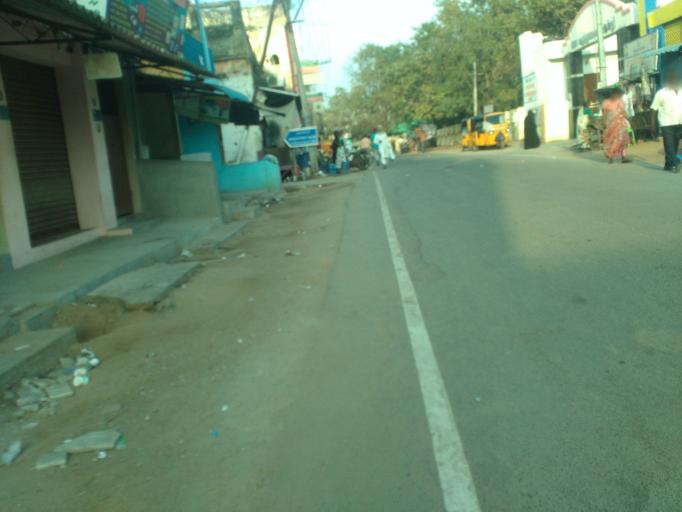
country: IN
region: Tamil Nadu
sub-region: Vellore
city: Ambur
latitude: 12.7864
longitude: 78.7174
